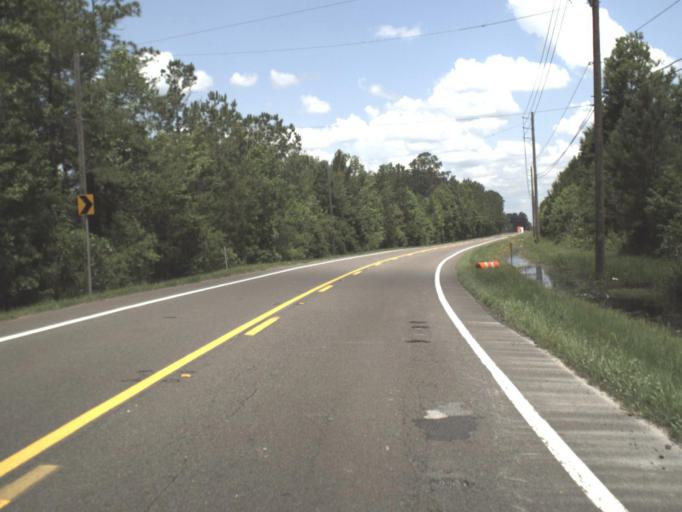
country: US
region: Florida
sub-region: Nassau County
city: Nassau Village-Ratliff
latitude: 30.4888
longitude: -81.7338
